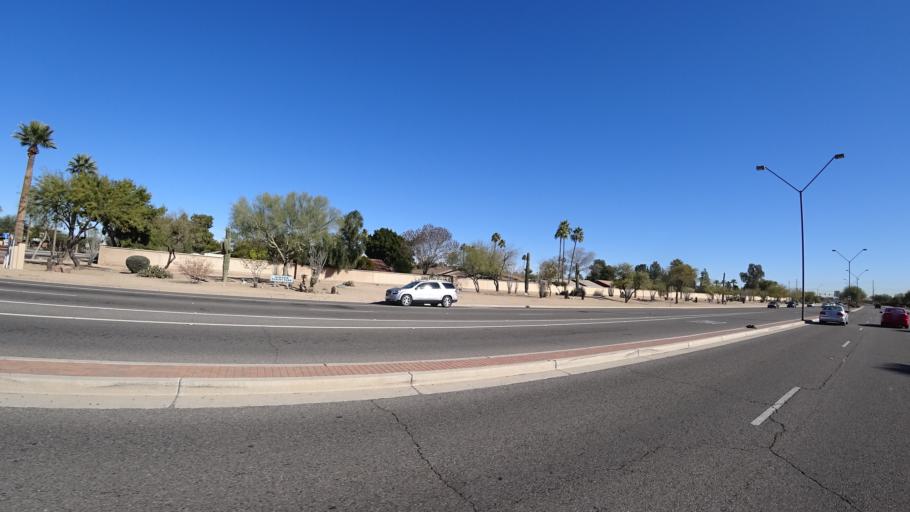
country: US
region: Arizona
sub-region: Maricopa County
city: Litchfield Park
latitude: 33.4857
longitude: -112.3622
